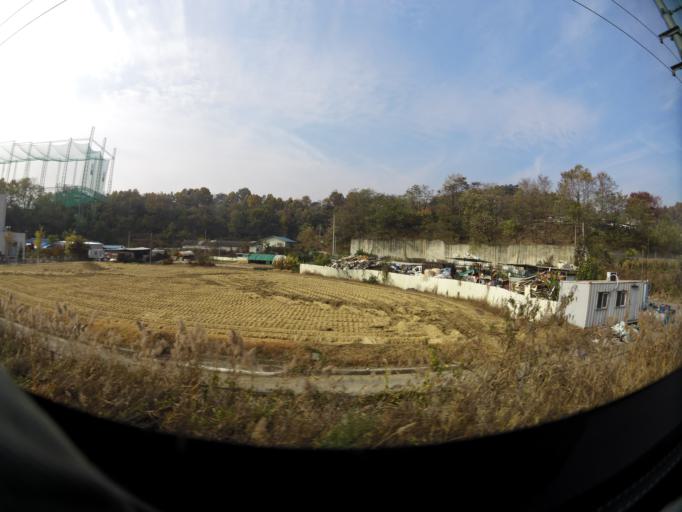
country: KR
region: Gyeongsangbuk-do
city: Gumi
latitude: 36.0780
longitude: 128.3570
